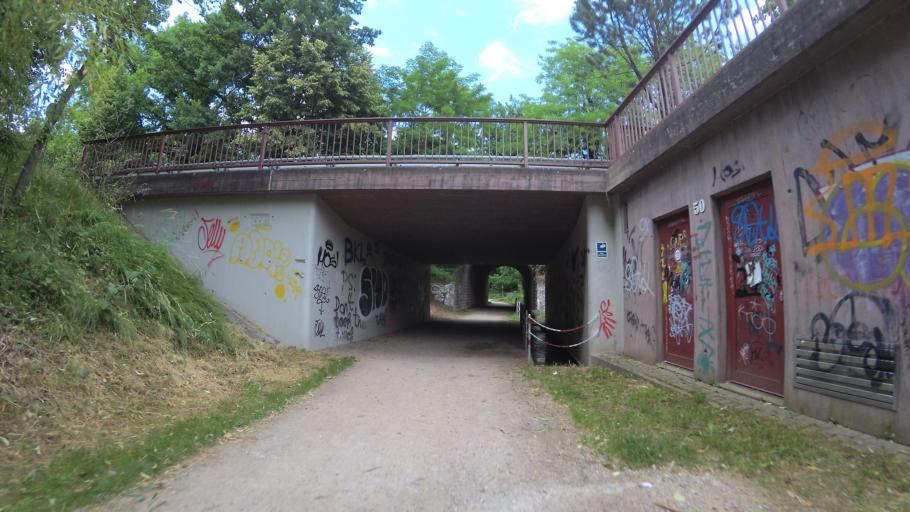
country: DE
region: Baden-Wuerttemberg
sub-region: Freiburg Region
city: Weil am Rhein
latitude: 47.5883
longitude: 7.6113
